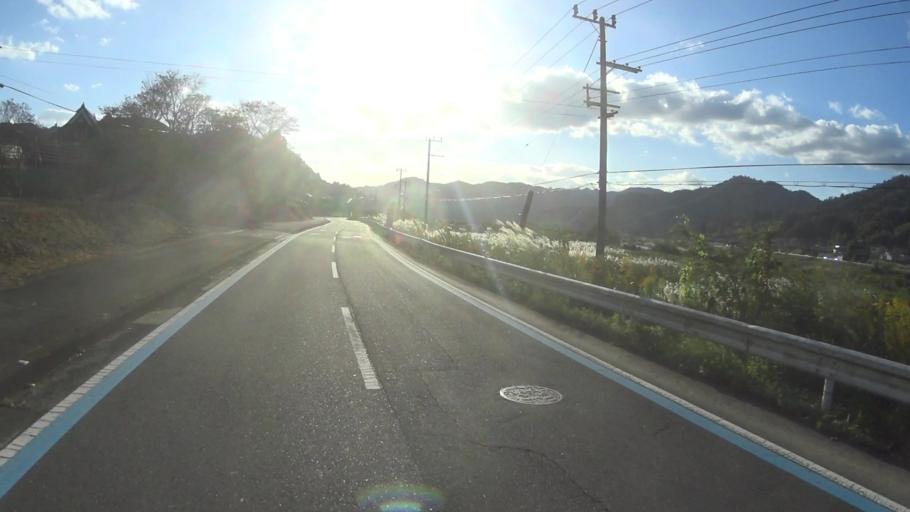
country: JP
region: Kyoto
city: Ayabe
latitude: 35.4105
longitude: 135.2004
